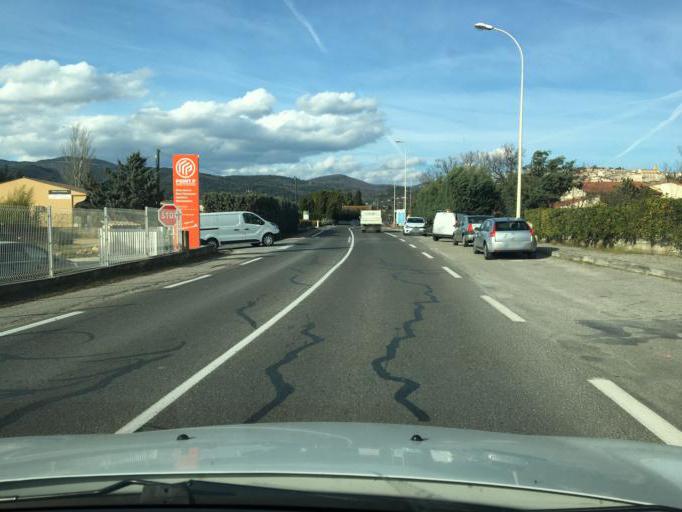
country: FR
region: Provence-Alpes-Cote d'Azur
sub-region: Departement du Var
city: Fayence
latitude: 43.6127
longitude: 6.6872
